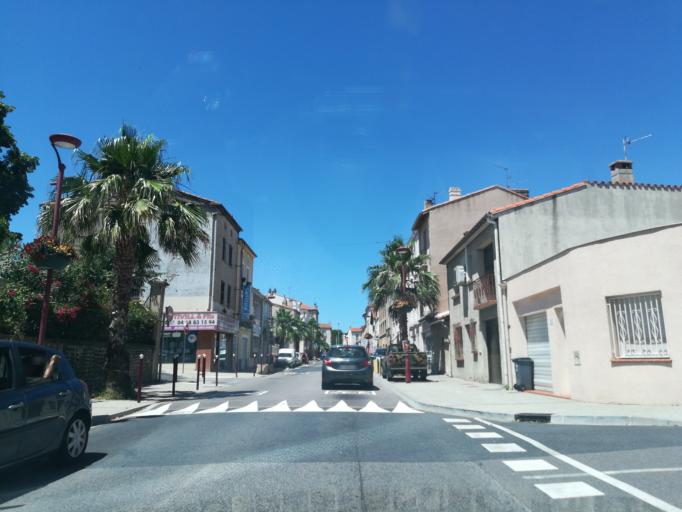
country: FR
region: Languedoc-Roussillon
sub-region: Departement des Pyrenees-Orientales
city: el Volo
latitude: 42.5233
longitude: 2.8319
